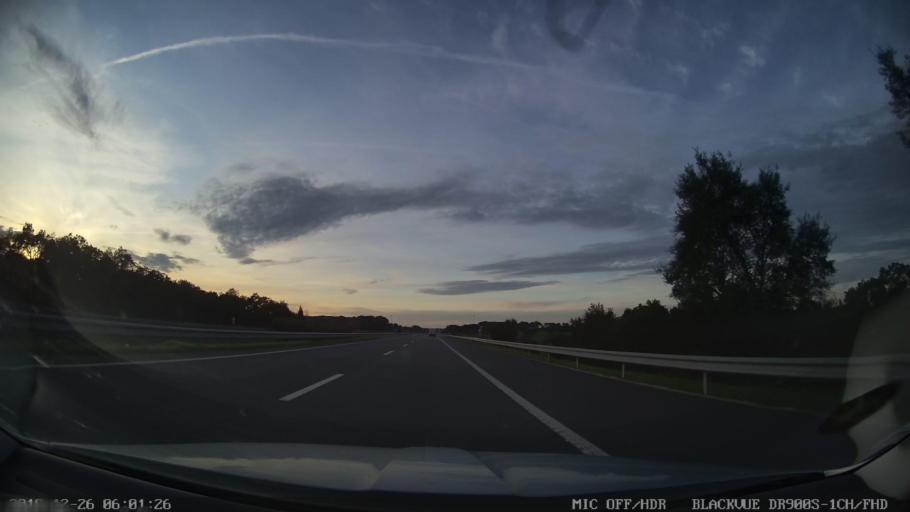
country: PT
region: Evora
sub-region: Arraiolos
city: Arraiolos
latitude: 38.6145
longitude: -8.0700
